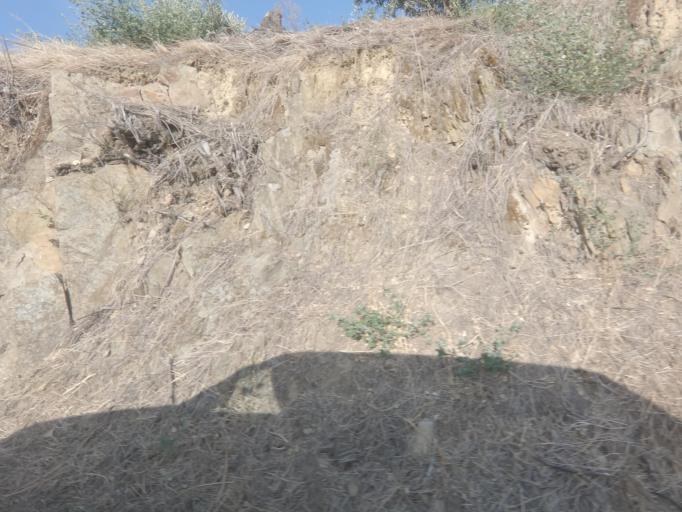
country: PT
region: Vila Real
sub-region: Sabrosa
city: Sabrosa
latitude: 41.2171
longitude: -7.5406
